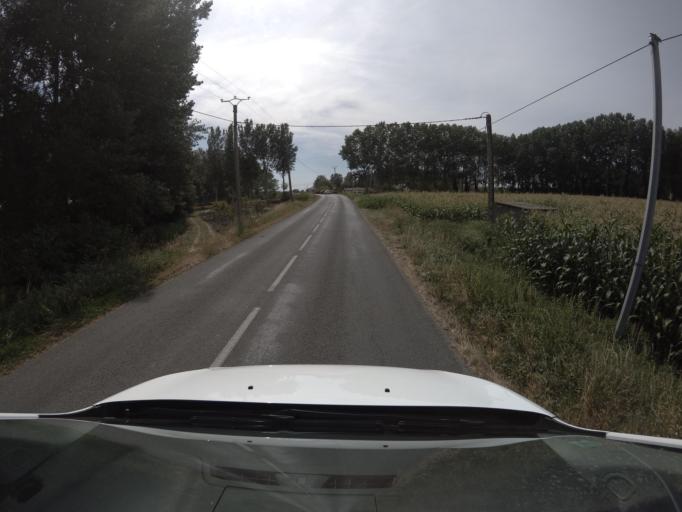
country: FR
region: Poitou-Charentes
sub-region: Departement des Deux-Sevres
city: Saint-Leger-de-Montbrun
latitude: 47.0088
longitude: -0.0735
